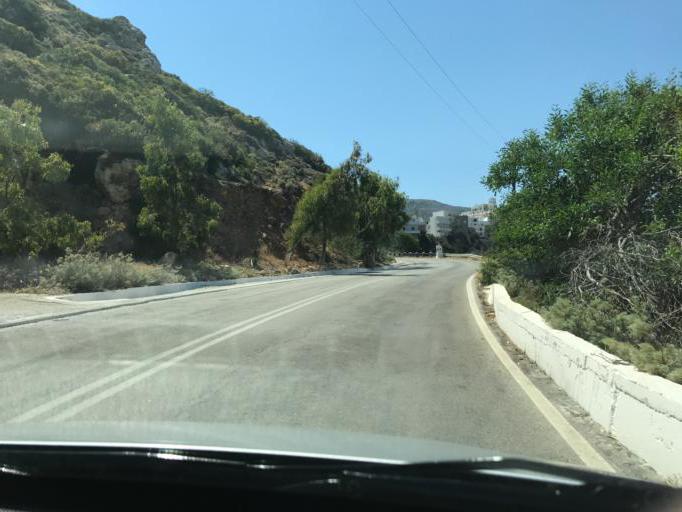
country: GR
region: South Aegean
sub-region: Nomos Dodekanisou
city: Karpathos
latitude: 35.4894
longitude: 27.1719
